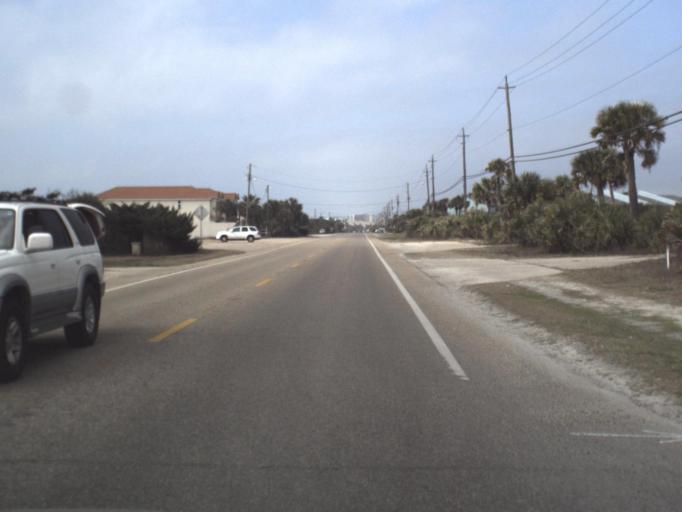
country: US
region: Florida
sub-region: Bay County
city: Laguna Beach
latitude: 30.2562
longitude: -85.9616
